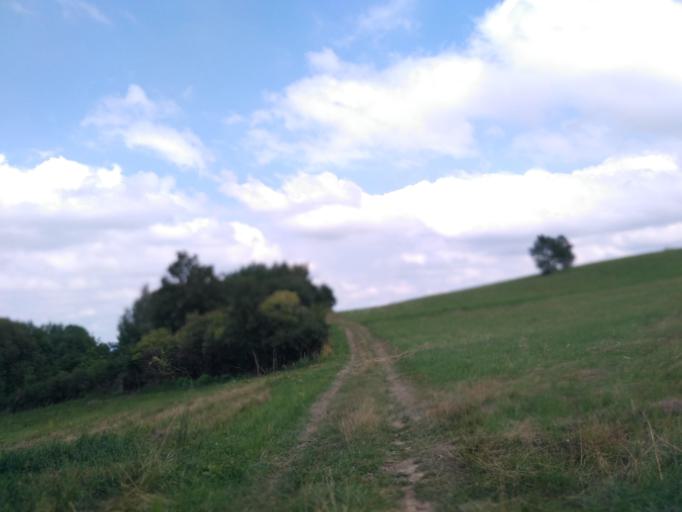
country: PL
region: Subcarpathian Voivodeship
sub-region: Powiat krosnienski
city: Iwonicz-Zdroj
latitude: 49.5814
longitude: 21.8064
